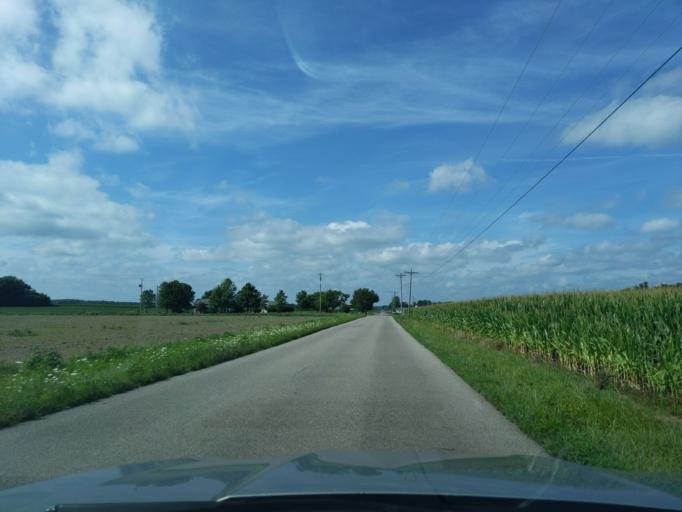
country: US
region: Indiana
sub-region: Ripley County
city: Batesville
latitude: 39.2925
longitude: -85.3477
